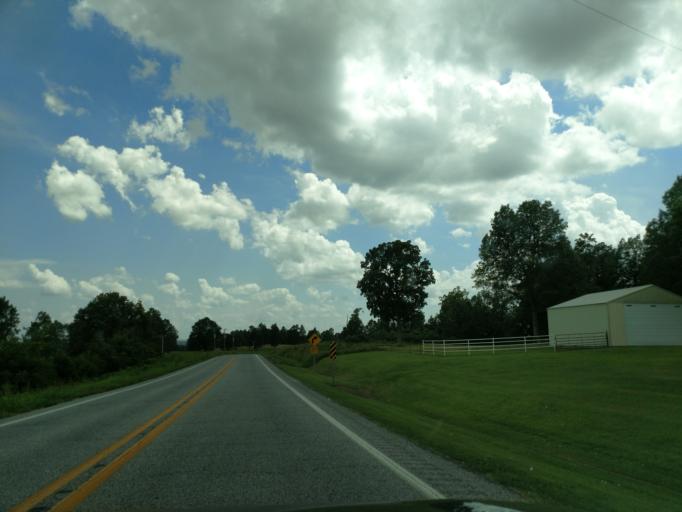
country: US
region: Arkansas
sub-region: Boone County
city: Harrison
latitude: 36.2076
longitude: -92.9337
